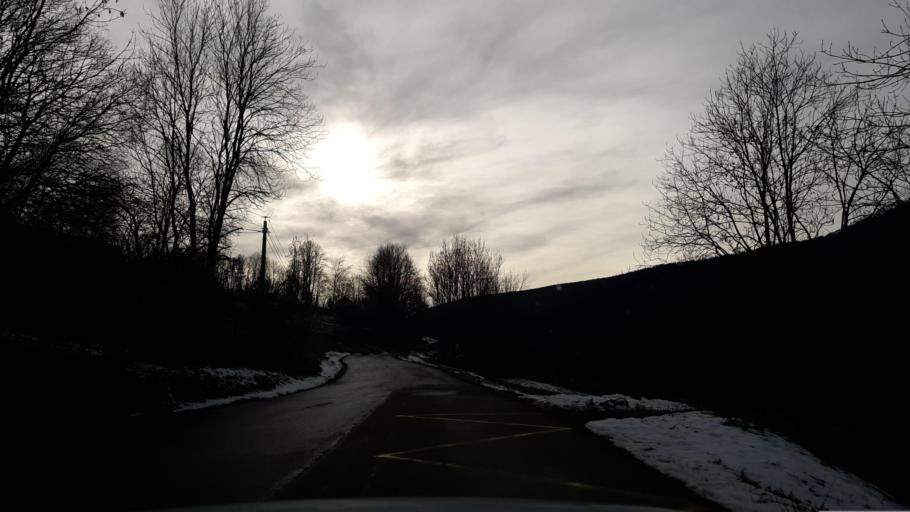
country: FR
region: Rhone-Alpes
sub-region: Departement de la Haute-Savoie
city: Cusy
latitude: 45.6629
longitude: 6.0969
